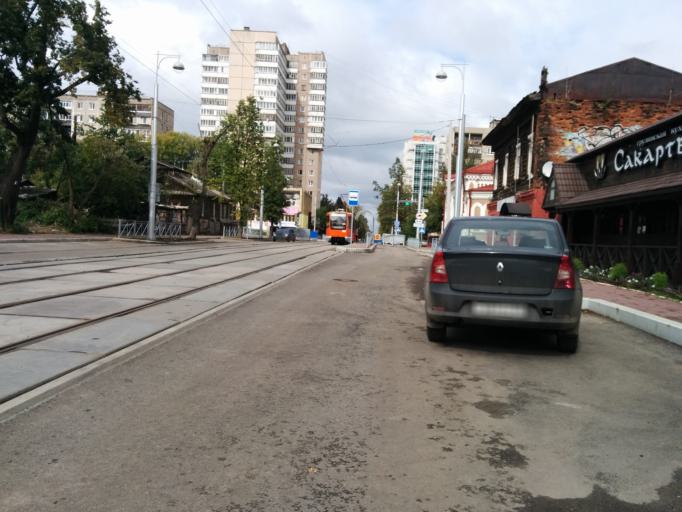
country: RU
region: Perm
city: Perm
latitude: 58.0096
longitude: 56.2579
